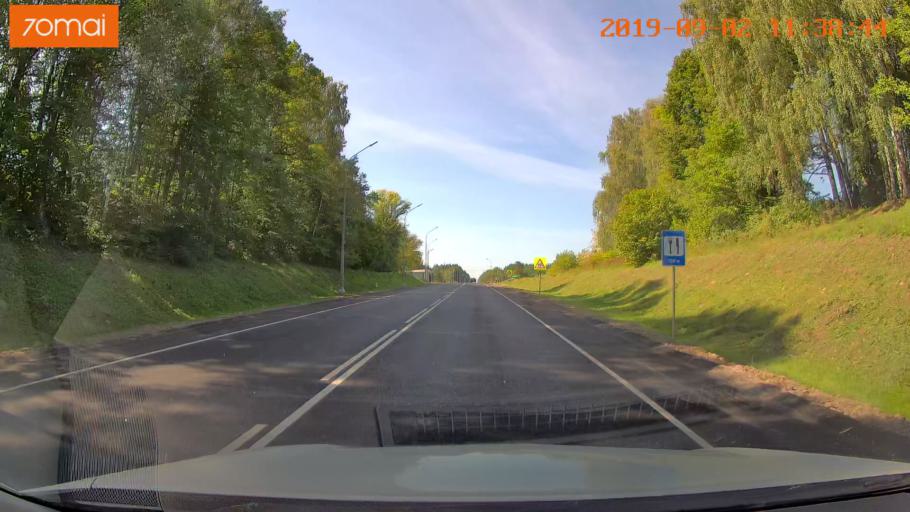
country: RU
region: Smolensk
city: Oster
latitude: 53.9116
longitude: 32.7349
